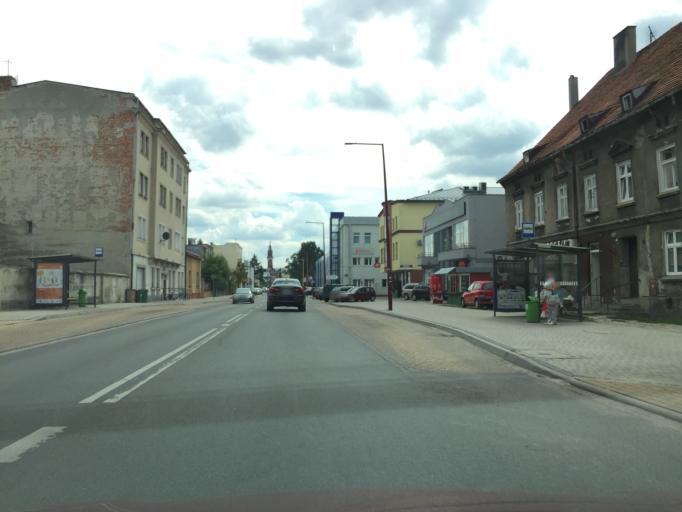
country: PL
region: Greater Poland Voivodeship
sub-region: Kalisz
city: Kalisz
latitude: 51.7550
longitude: 18.0940
